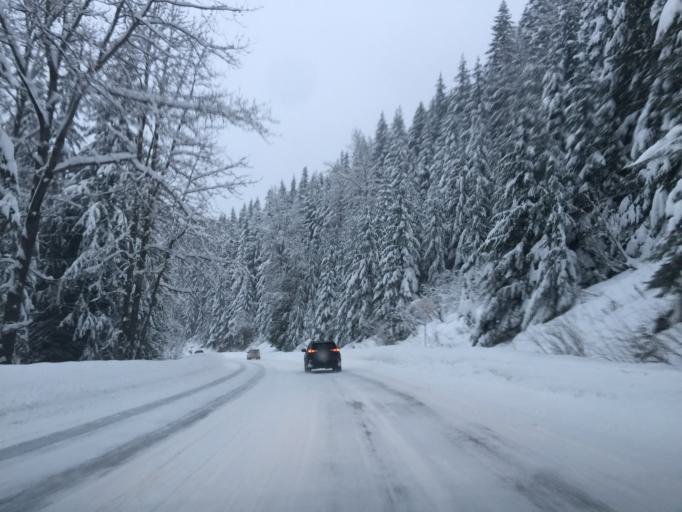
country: US
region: Washington
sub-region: Chelan County
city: Leavenworth
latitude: 47.7671
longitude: -120.9878
